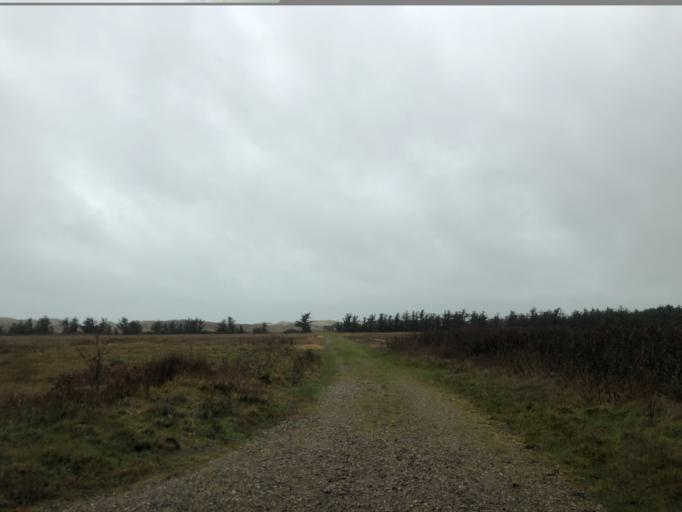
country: DK
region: Central Jutland
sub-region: Holstebro Kommune
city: Ulfborg
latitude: 56.2787
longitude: 8.1436
